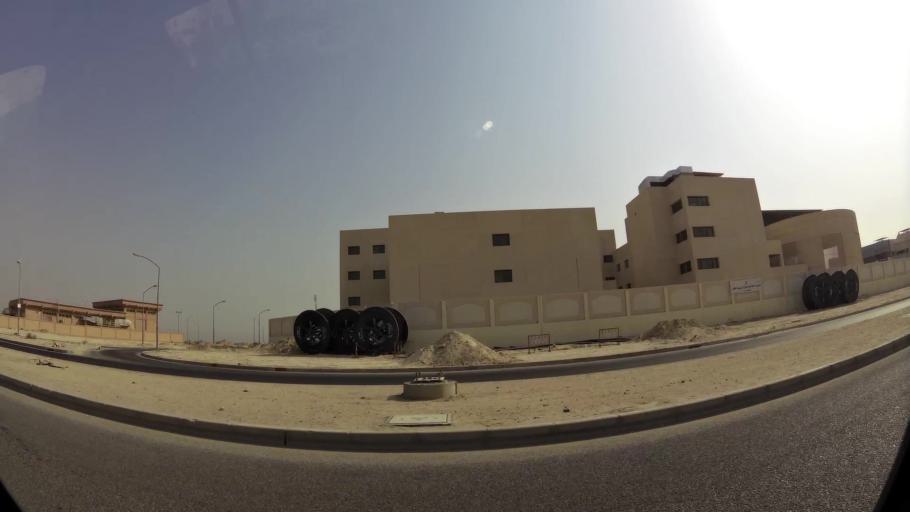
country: KW
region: Muhafazat al Jahra'
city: Al Jahra'
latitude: 29.3597
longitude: 47.7548
